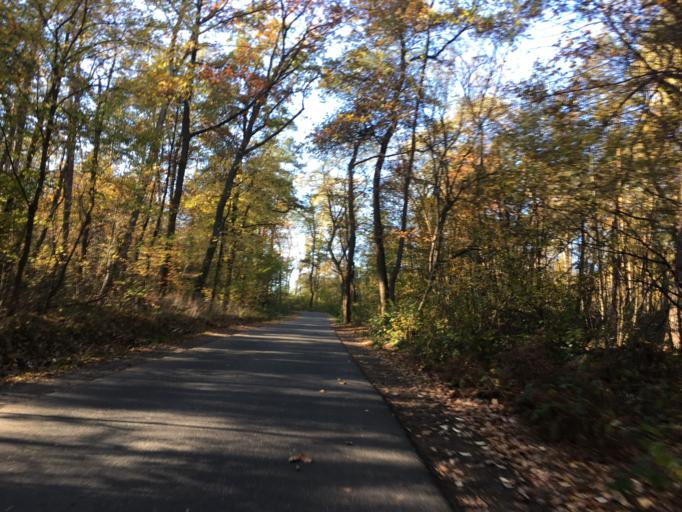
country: DE
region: Brandenburg
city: Bad Saarow
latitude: 52.2929
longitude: 14.0295
